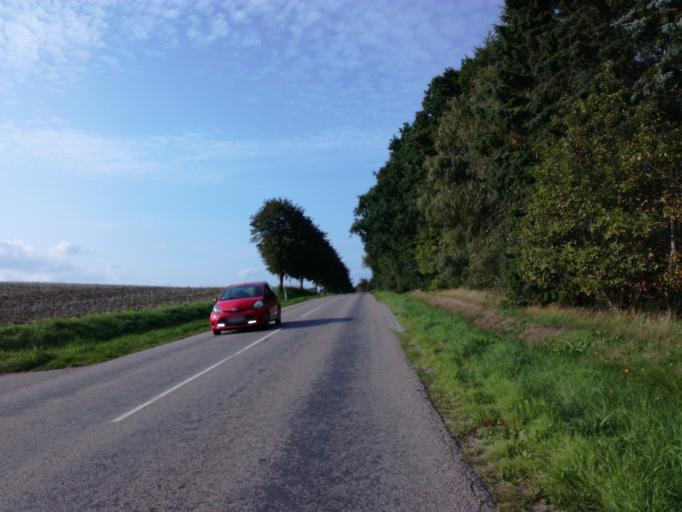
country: DK
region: South Denmark
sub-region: Vejle Kommune
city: Borkop
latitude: 55.6497
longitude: 9.6438
